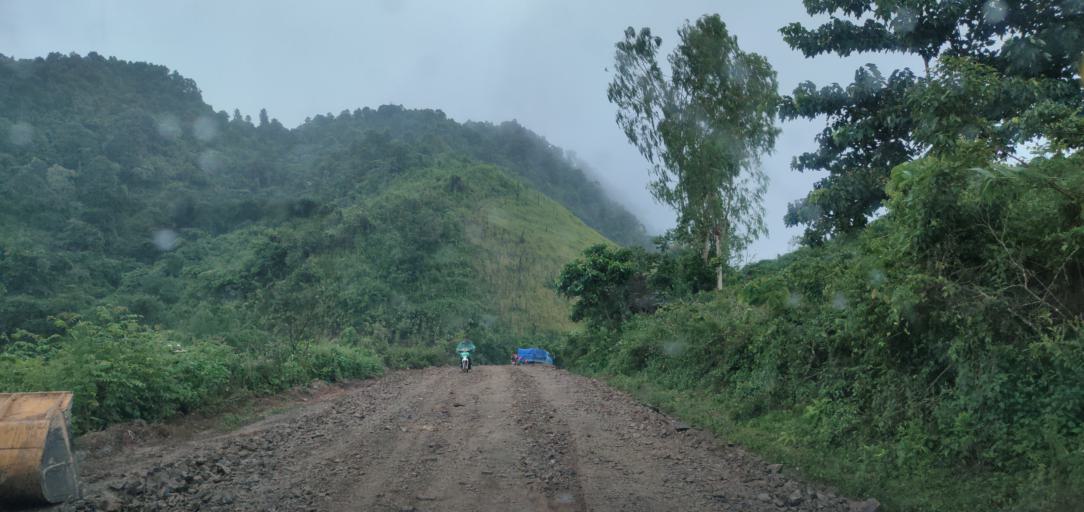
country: LA
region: Phongsali
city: Phongsali
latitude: 21.4310
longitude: 102.1606
